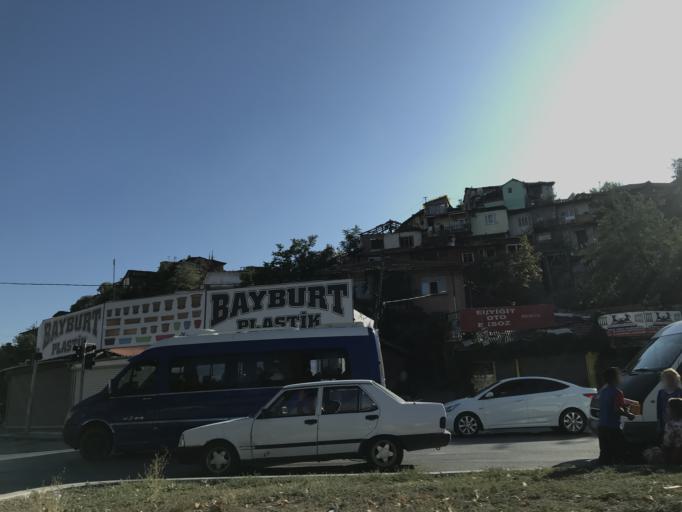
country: TR
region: Ankara
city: Cankaya
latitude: 39.9417
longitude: 32.8714
